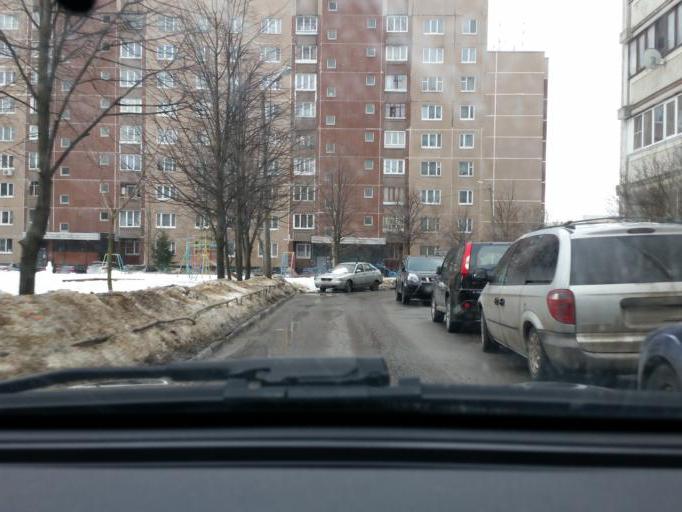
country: RU
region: Moskovskaya
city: Shcherbinka
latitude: 55.5348
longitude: 37.5859
